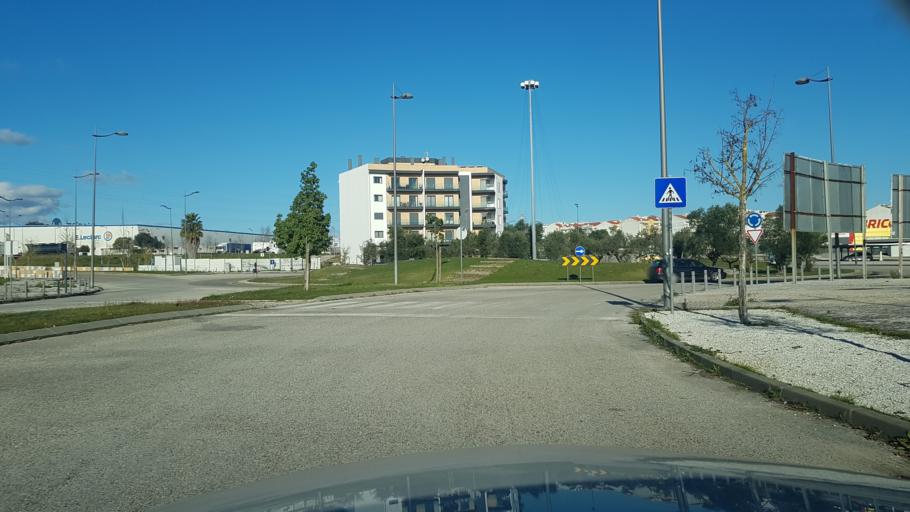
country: PT
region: Santarem
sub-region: Entroncamento
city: Entroncamento
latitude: 39.4719
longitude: -8.4862
